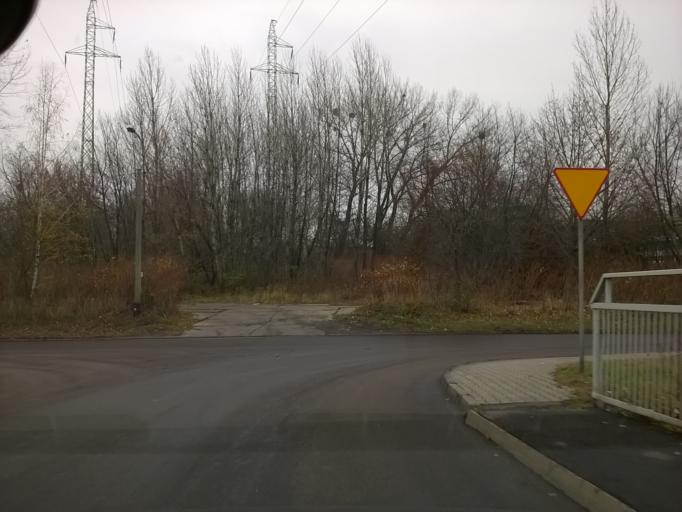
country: PL
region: Silesian Voivodeship
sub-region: Chorzow
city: Chorzow
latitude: 50.3110
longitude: 18.9710
